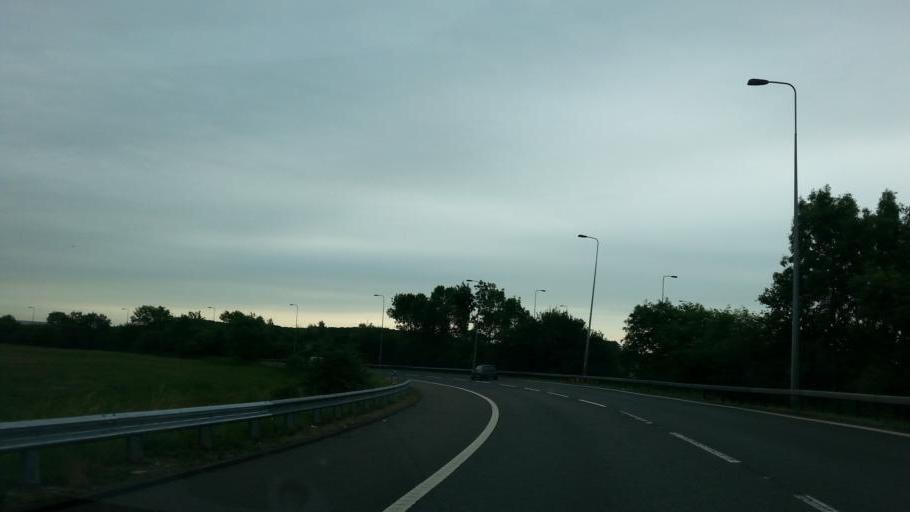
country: GB
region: England
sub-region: Warwickshire
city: Brandon
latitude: 52.4342
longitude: -1.4221
